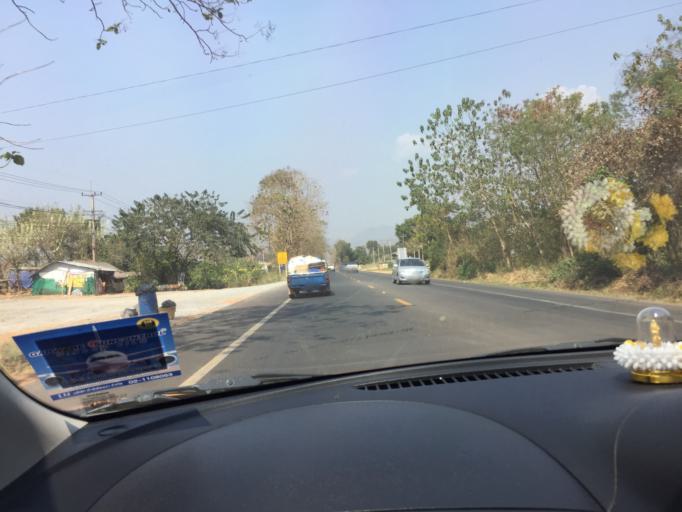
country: TH
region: Kanchanaburi
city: Sai Yok
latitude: 14.1727
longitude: 99.1299
